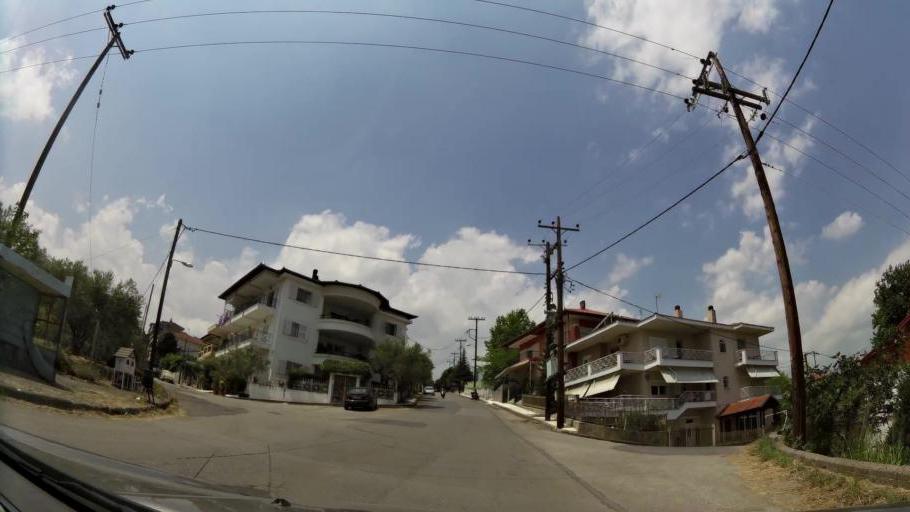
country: GR
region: Central Macedonia
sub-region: Nomos Imathias
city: Veroia
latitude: 40.5137
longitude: 22.1895
